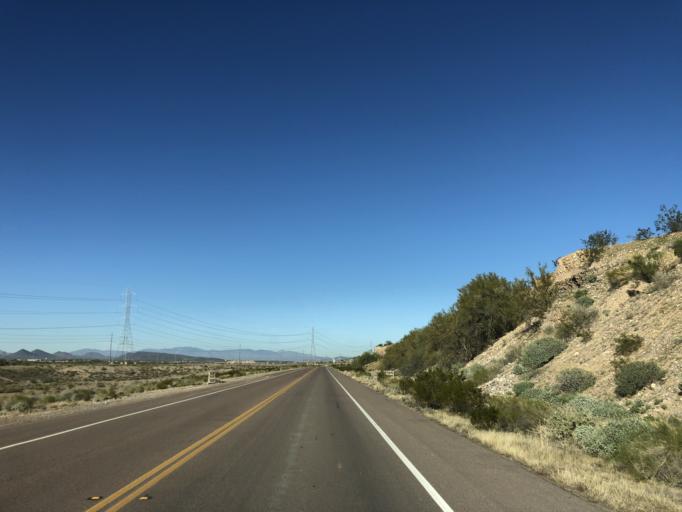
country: US
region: Arizona
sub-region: Maricopa County
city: Sun City West
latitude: 33.6834
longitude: -112.2975
